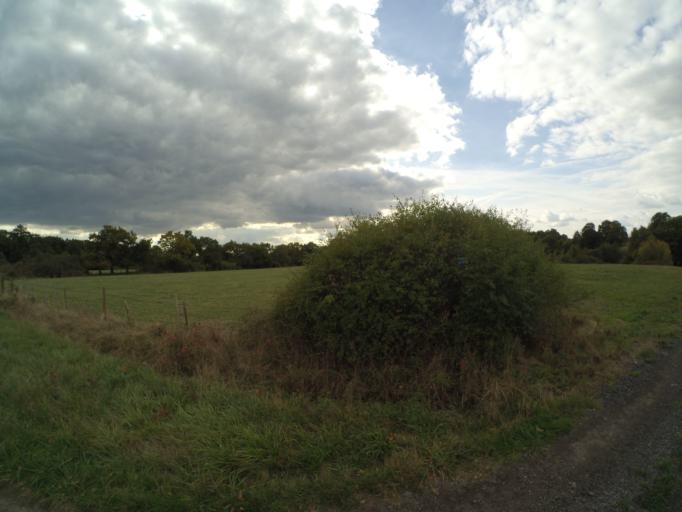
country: FR
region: Pays de la Loire
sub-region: Departement de la Loire-Atlantique
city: Remouille
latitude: 47.0712
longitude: -1.3721
